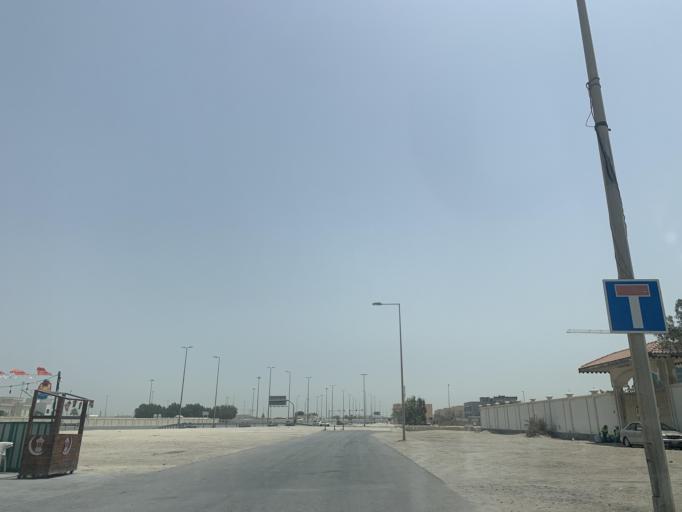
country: BH
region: Northern
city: Madinat `Isa
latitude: 26.1593
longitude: 50.5244
